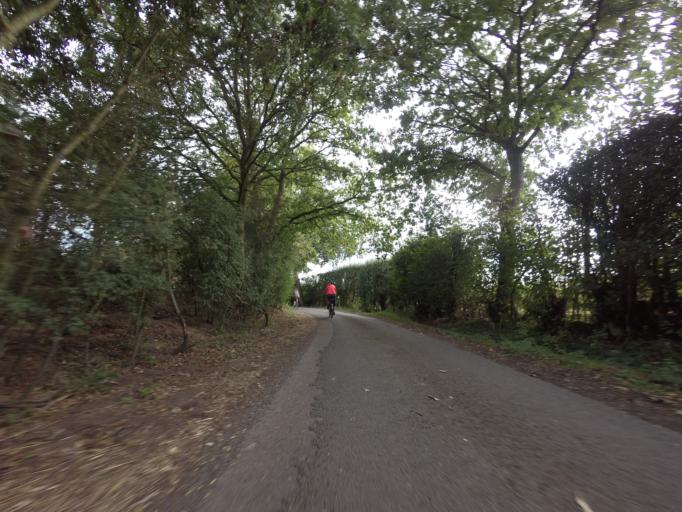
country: GB
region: England
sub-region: Kent
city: Staplehurst
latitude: 51.1915
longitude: 0.5760
